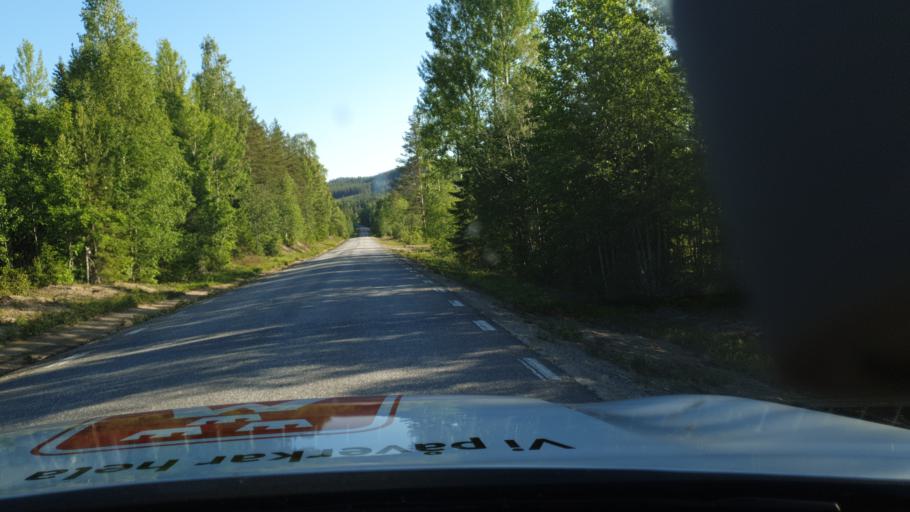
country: SE
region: Vaesterbotten
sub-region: Vannas Kommun
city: Vannasby
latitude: 64.0646
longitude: 20.0642
